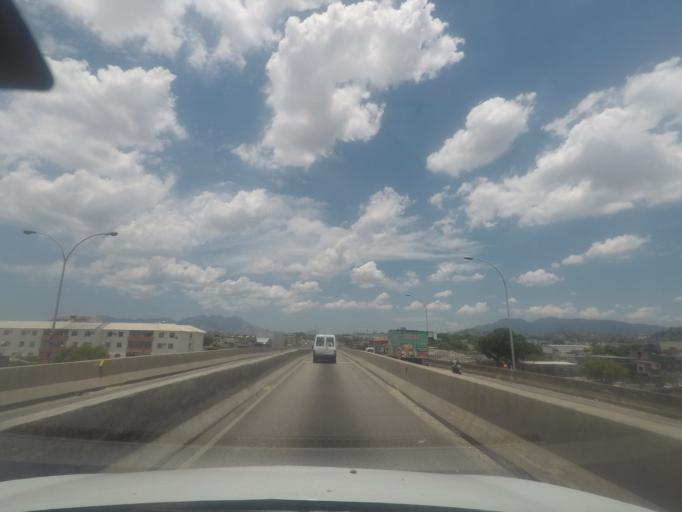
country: BR
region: Rio de Janeiro
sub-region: Sao Joao De Meriti
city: Sao Joao de Meriti
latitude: -22.8293
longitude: -43.3462
